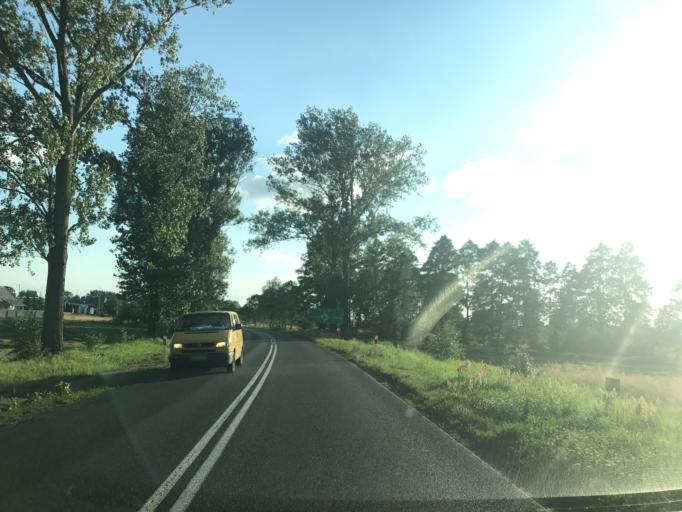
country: PL
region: Greater Poland Voivodeship
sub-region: Powiat pleszewski
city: Gizalki
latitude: 52.0468
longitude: 17.7679
